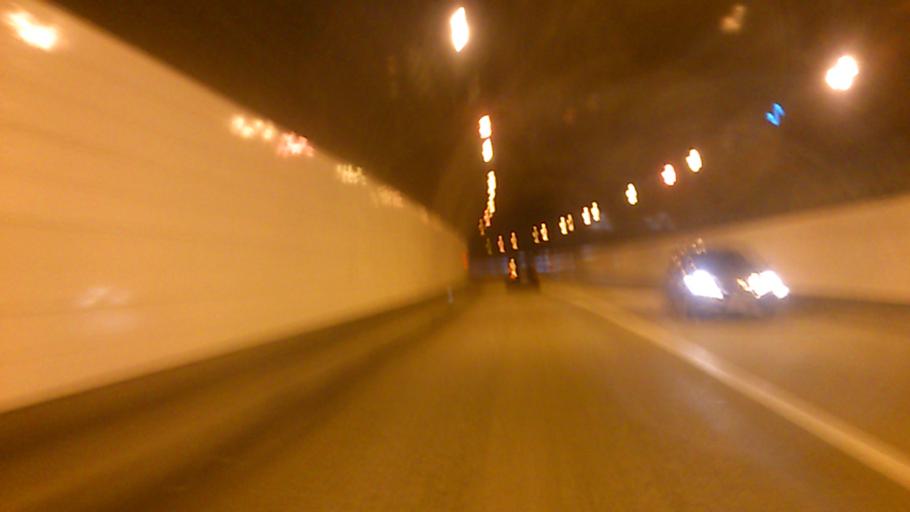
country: JP
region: Akita
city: Takanosu
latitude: 40.2185
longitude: 140.2396
